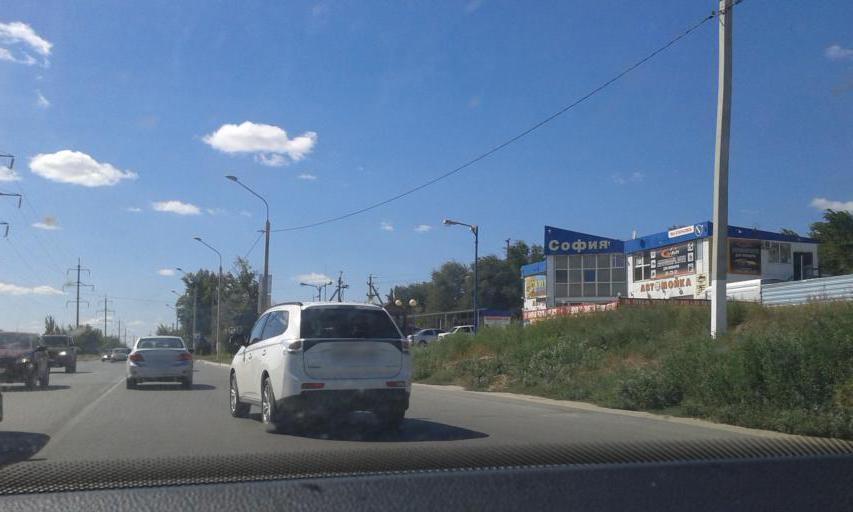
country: RU
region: Volgograd
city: Volgograd
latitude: 48.6737
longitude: 44.4608
